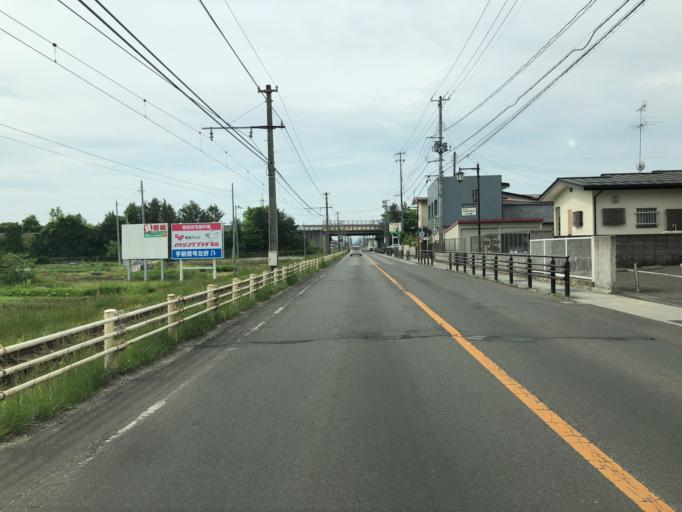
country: JP
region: Fukushima
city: Fukushima-shi
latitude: 37.8025
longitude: 140.4421
